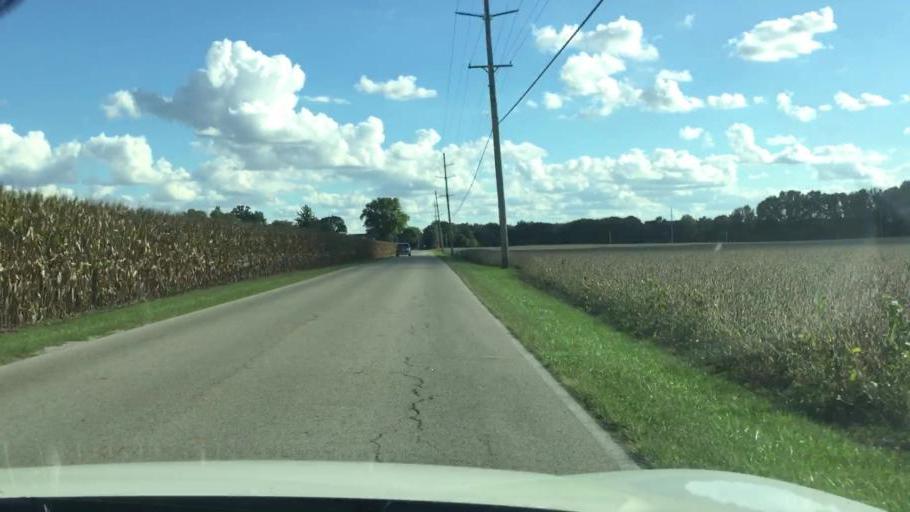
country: US
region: Ohio
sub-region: Clark County
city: Northridge
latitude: 39.9429
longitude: -83.7102
